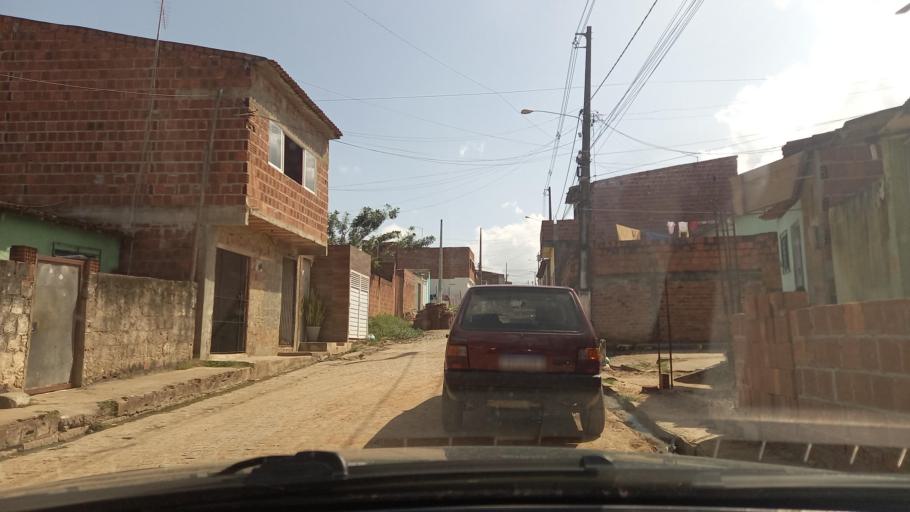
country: BR
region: Pernambuco
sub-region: Goiana
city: Goiana
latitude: -7.5675
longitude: -35.0144
